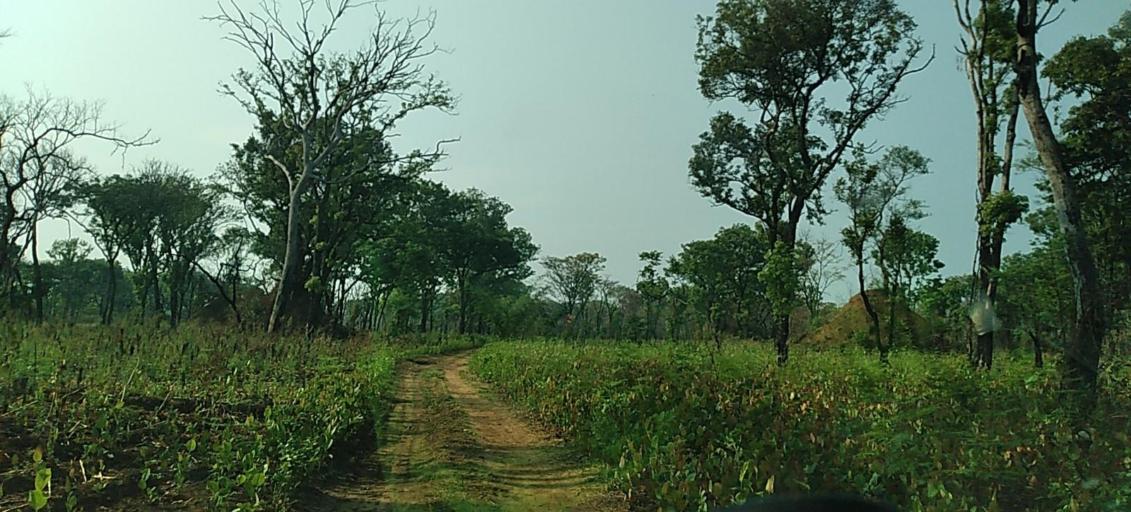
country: ZM
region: North-Western
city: Solwezi
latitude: -12.4036
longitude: 26.5866
